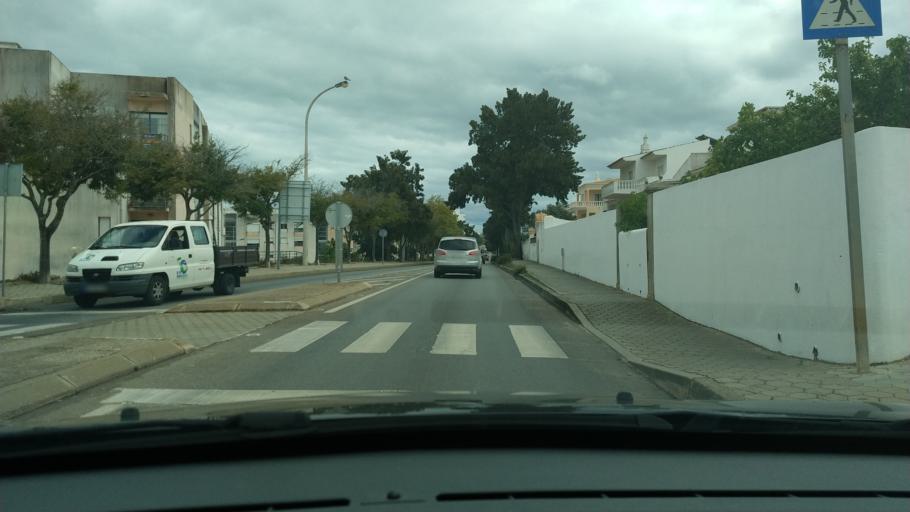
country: PT
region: Faro
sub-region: Lagos
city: Lagos
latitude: 37.1011
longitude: -8.6874
